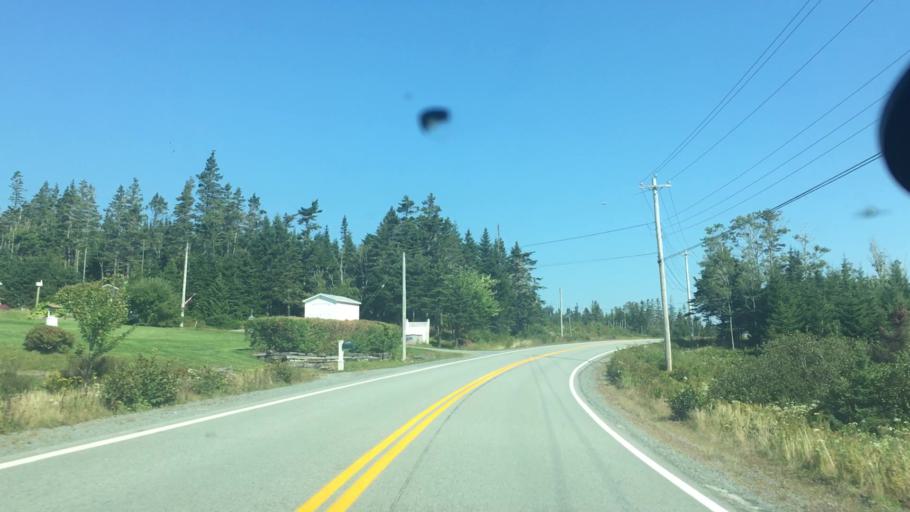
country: CA
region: Nova Scotia
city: New Glasgow
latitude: 44.9277
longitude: -62.2983
